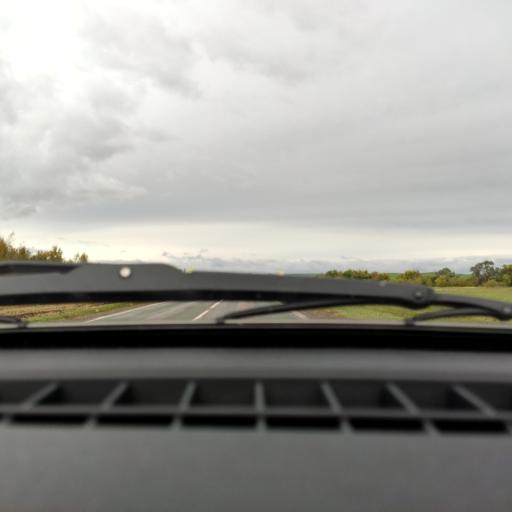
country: RU
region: Bashkortostan
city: Rayevskiy
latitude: 54.1346
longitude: 54.9398
